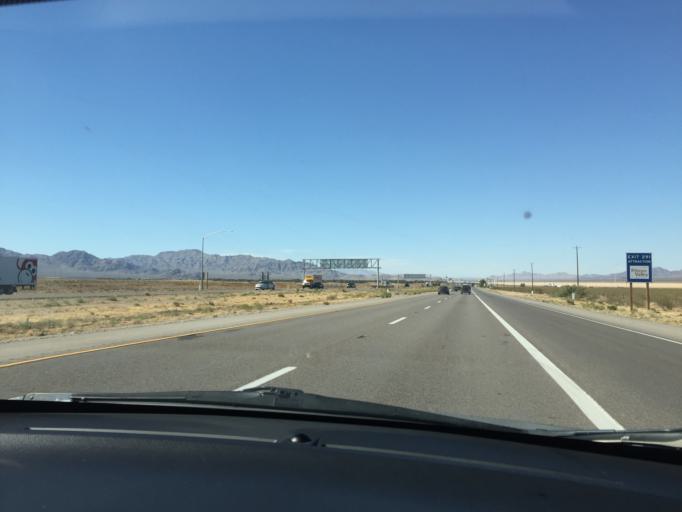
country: US
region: Nevada
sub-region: Clark County
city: Sandy Valley
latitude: 35.5278
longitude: -115.4251
